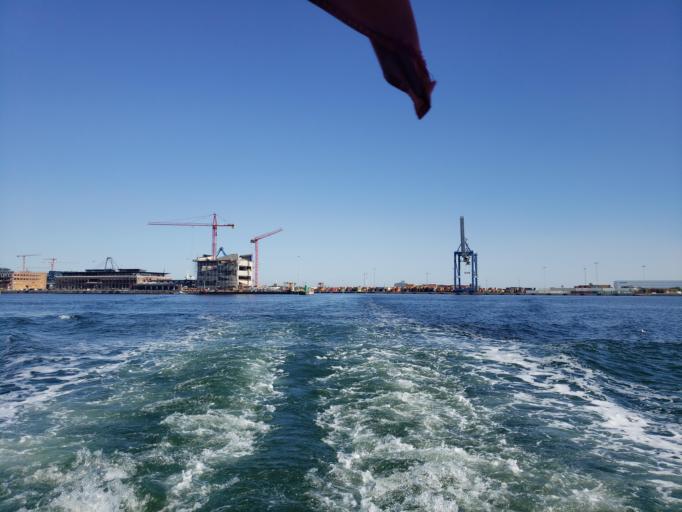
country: DK
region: Capital Region
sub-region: Kobenhavn
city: Christianshavn
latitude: 55.7049
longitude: 12.6060
